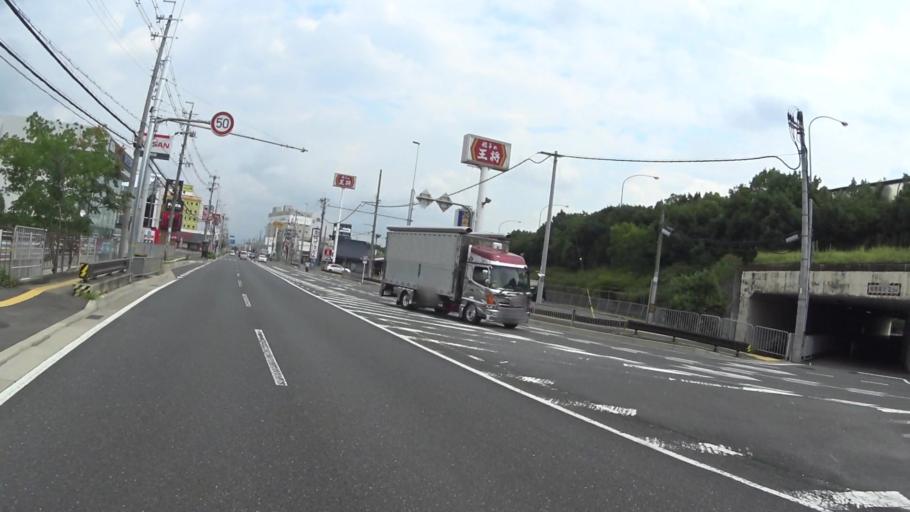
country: JP
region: Kyoto
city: Muko
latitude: 34.9456
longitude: 135.7168
